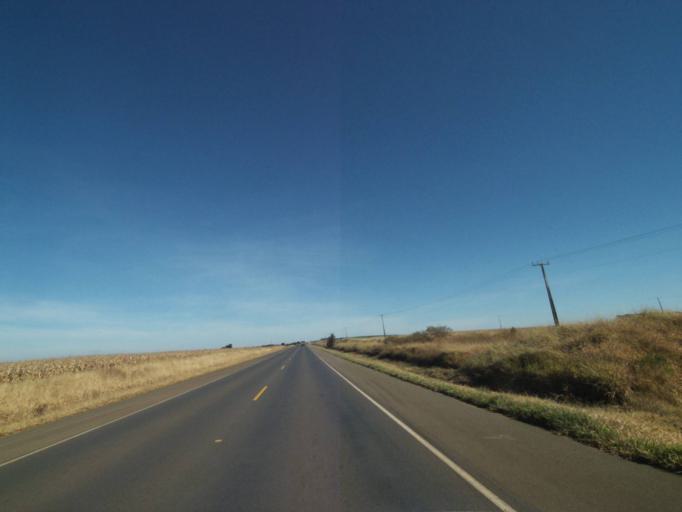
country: BR
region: Parana
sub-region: Tibagi
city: Tibagi
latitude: -24.3521
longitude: -50.3144
